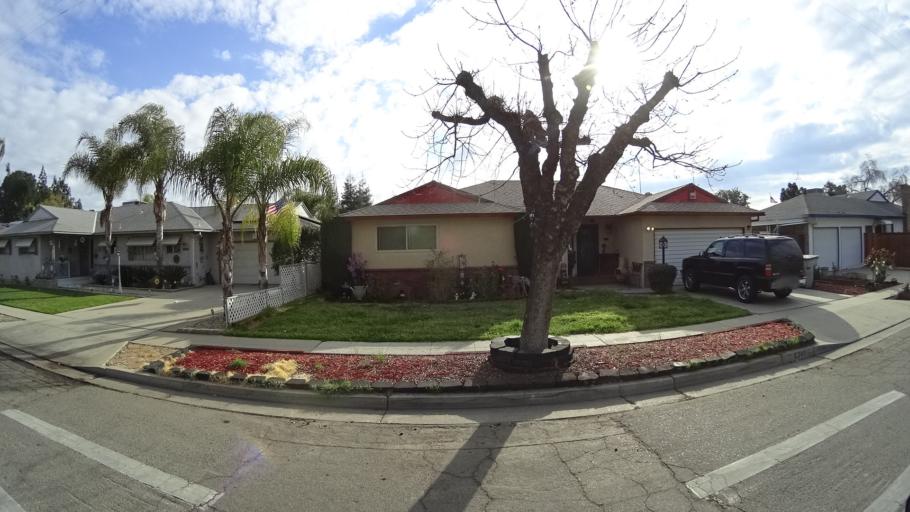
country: US
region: California
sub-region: Fresno County
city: Clovis
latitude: 36.8293
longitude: -119.7677
